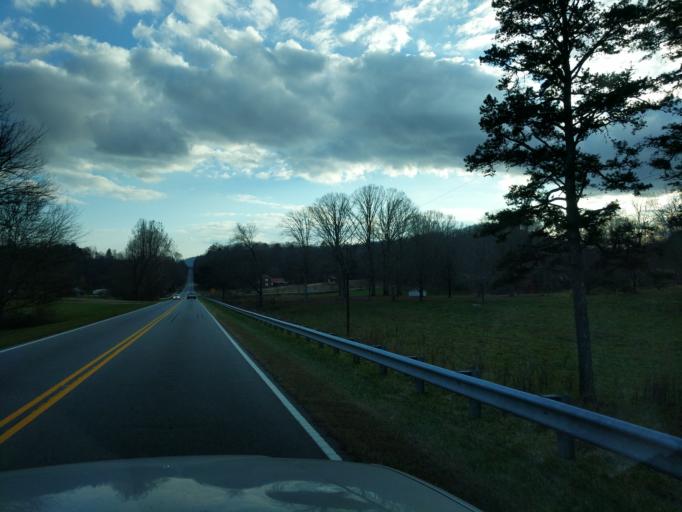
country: US
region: North Carolina
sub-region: McDowell County
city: West Marion
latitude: 35.6140
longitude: -81.9854
